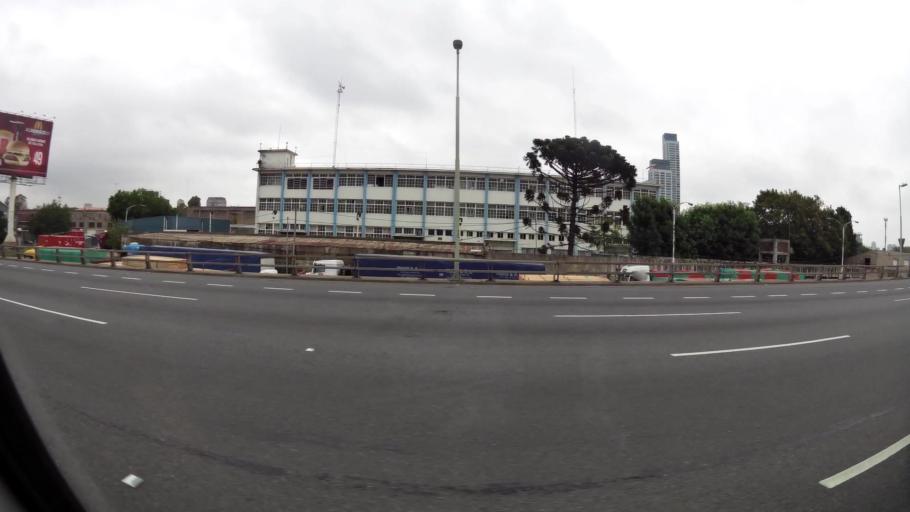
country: AR
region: Buenos Aires F.D.
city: Retiro
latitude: -34.5724
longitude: -58.3994
